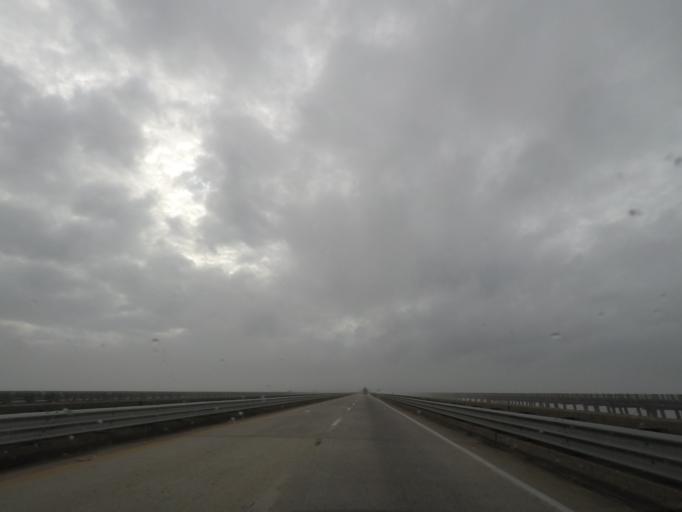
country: US
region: South Carolina
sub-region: Orangeburg County
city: Holly Hill
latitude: 33.5084
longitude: -80.4490
